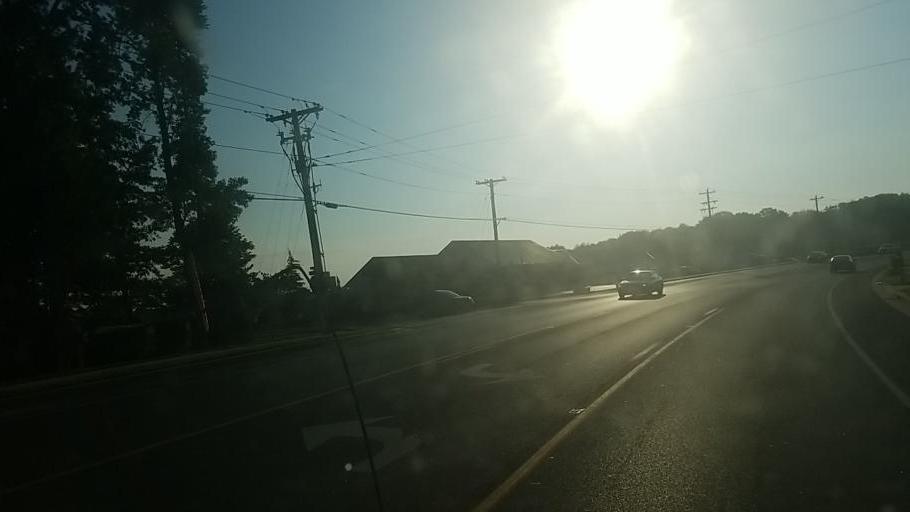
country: US
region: Delaware
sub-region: Sussex County
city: Ocean View
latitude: 38.4732
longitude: -75.1017
